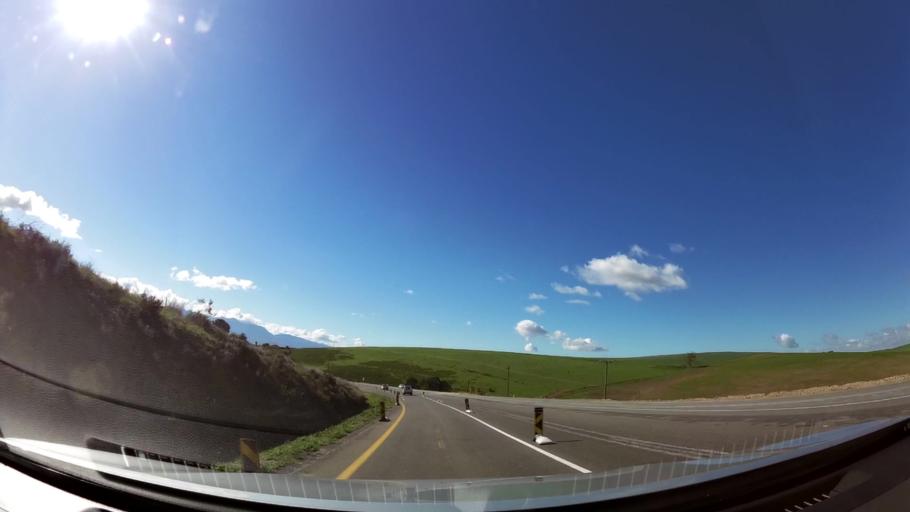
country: ZA
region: Western Cape
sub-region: Overberg District Municipality
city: Caledon
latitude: -34.2047
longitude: 19.5995
